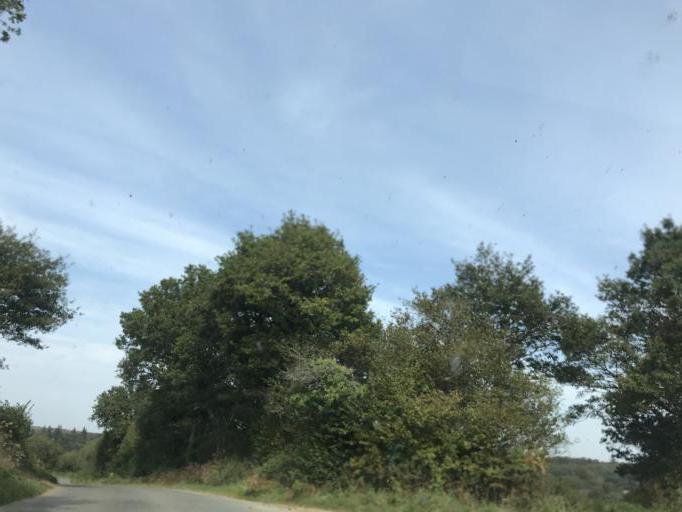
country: FR
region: Brittany
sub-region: Departement du Finistere
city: Brasparts
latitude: 48.3324
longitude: -3.9005
